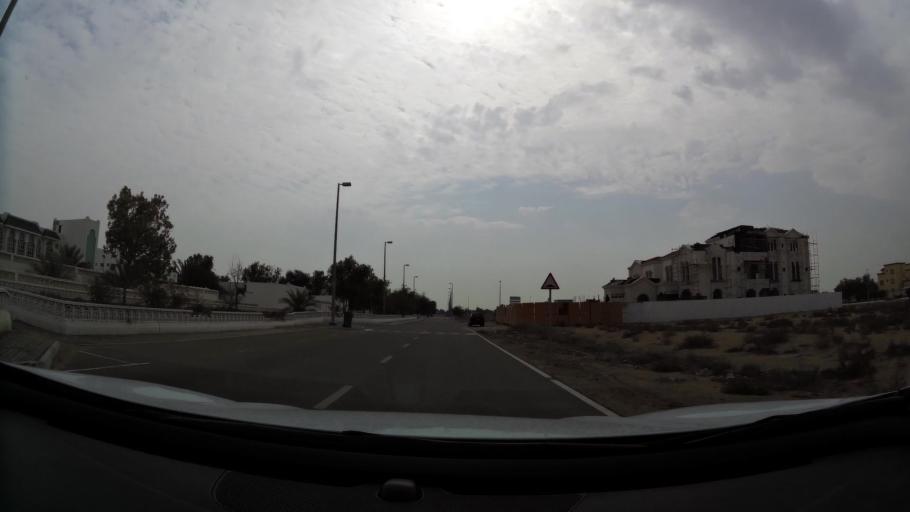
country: AE
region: Abu Dhabi
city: Abu Dhabi
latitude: 24.6362
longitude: 54.7210
